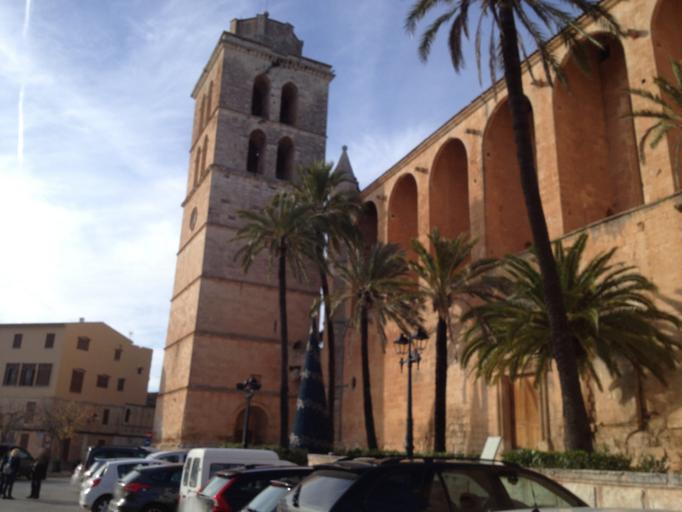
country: ES
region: Balearic Islands
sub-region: Illes Balears
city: Muro
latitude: 39.7370
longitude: 3.0577
